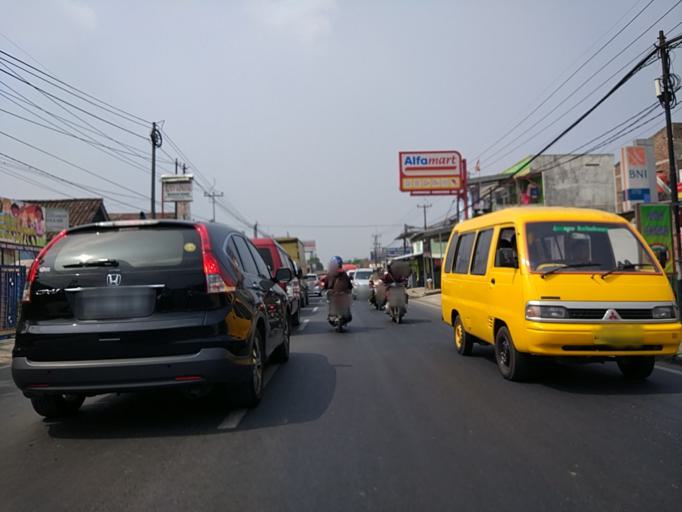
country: ID
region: West Java
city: Padalarang
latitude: -6.8363
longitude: 107.4717
